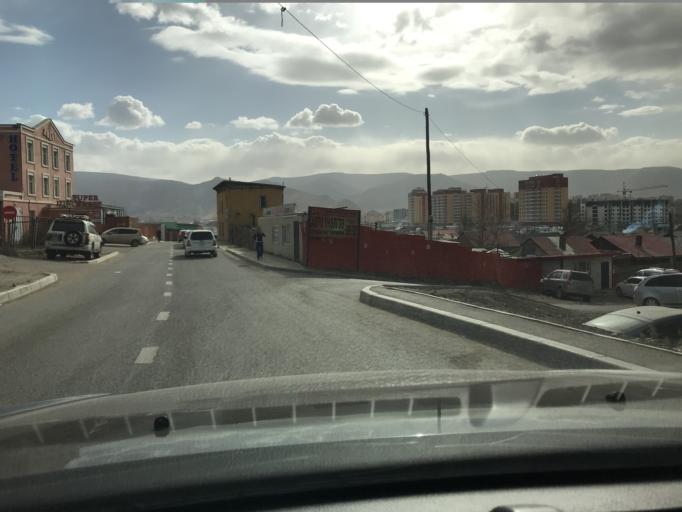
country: MN
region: Ulaanbaatar
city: Ulaanbaatar
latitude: 47.9157
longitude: 106.9640
